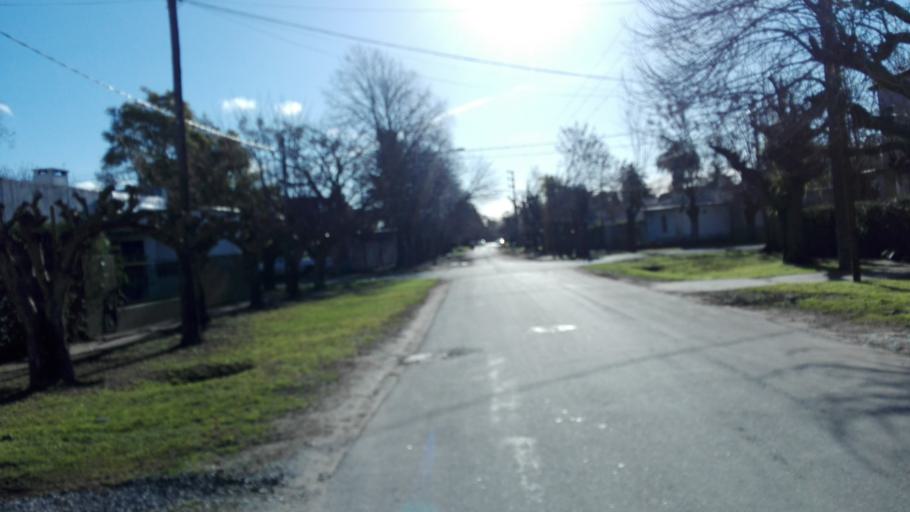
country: AR
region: Buenos Aires
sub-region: Partido de La Plata
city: La Plata
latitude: -34.8802
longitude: -58.0034
